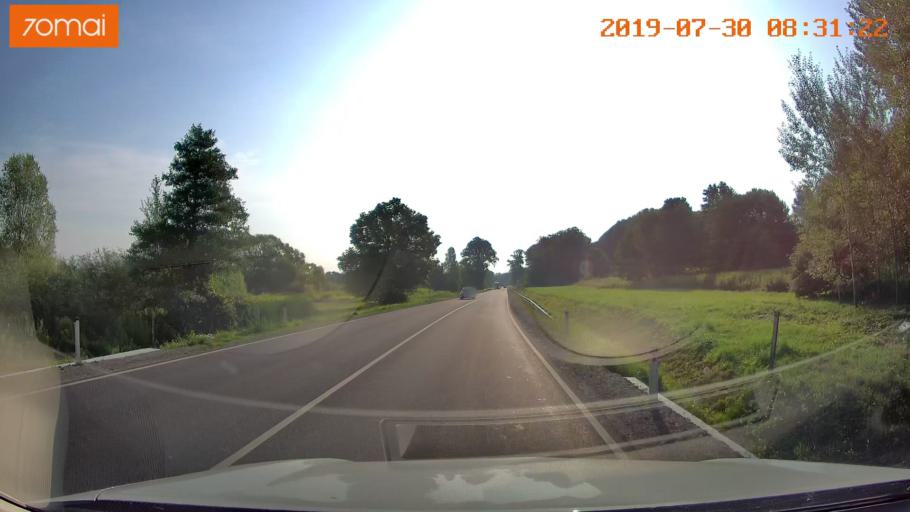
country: RU
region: Kaliningrad
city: Chernyakhovsk
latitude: 54.6376
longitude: 21.7054
